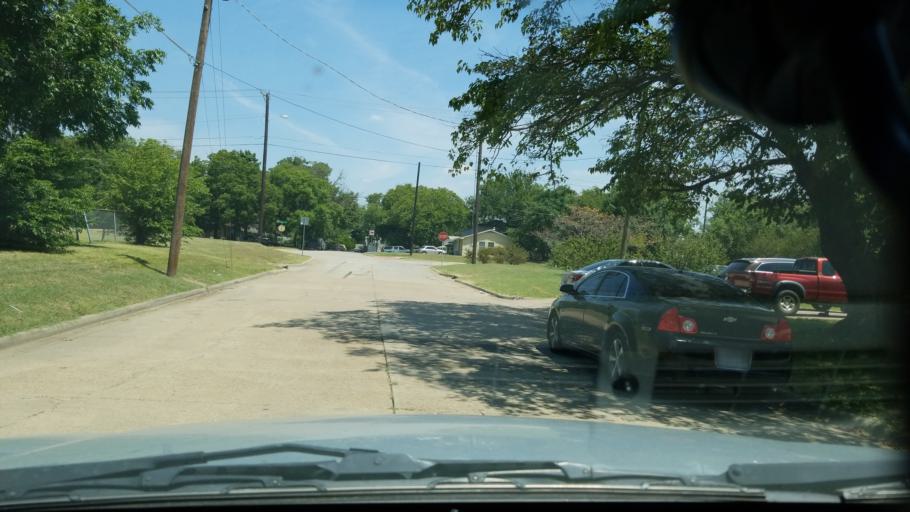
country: US
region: Texas
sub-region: Dallas County
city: Grand Prairie
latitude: 32.7596
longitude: -96.9584
